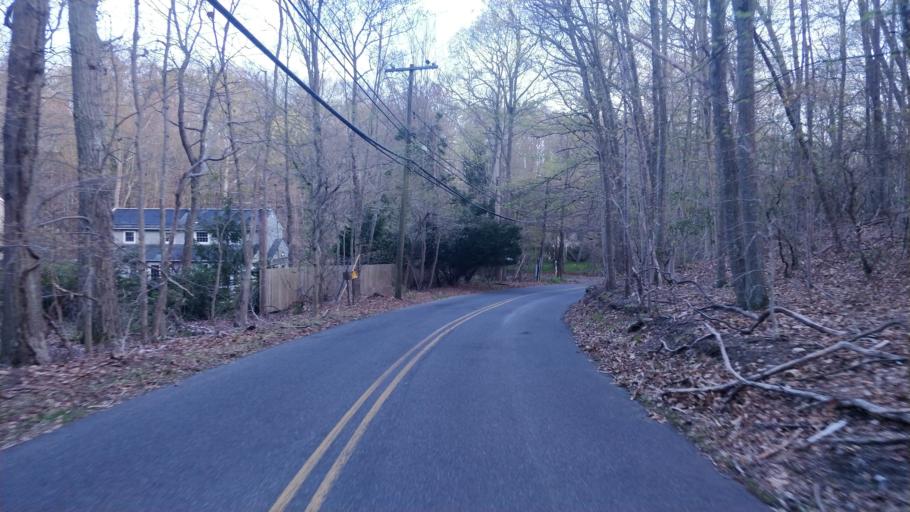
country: US
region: New York
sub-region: Suffolk County
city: Village of the Branch
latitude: 40.8818
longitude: -73.1848
